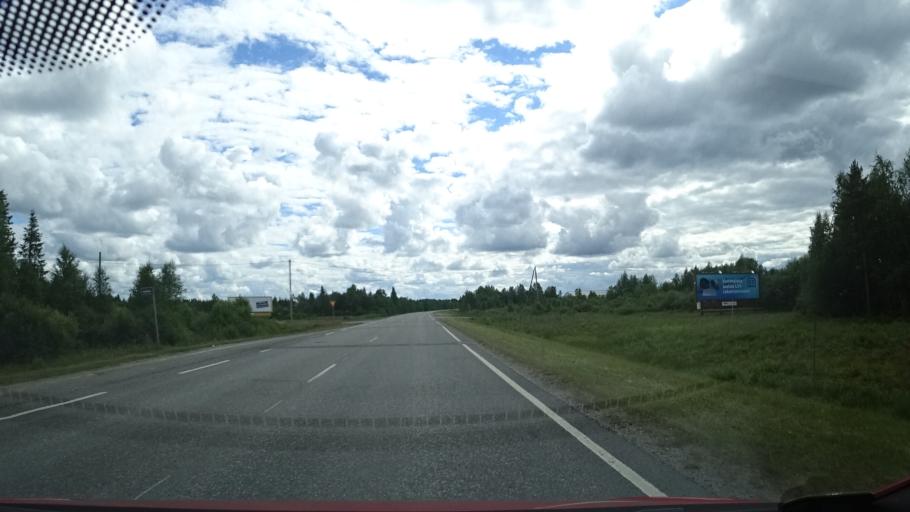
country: FI
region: Lapland
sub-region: Tunturi-Lappi
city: Kittilae
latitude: 67.6374
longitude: 24.9240
